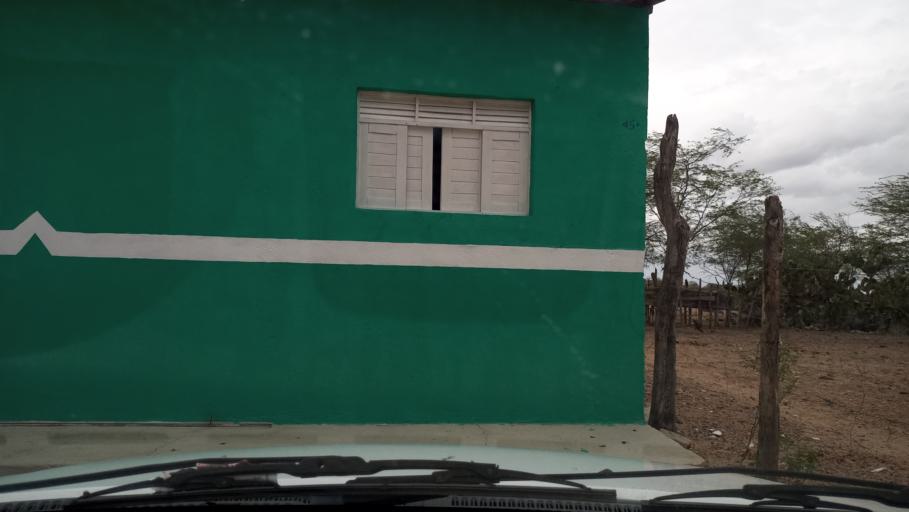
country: BR
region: Rio Grande do Norte
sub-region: Tangara
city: Tangara
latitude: -6.1910
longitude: -35.7990
